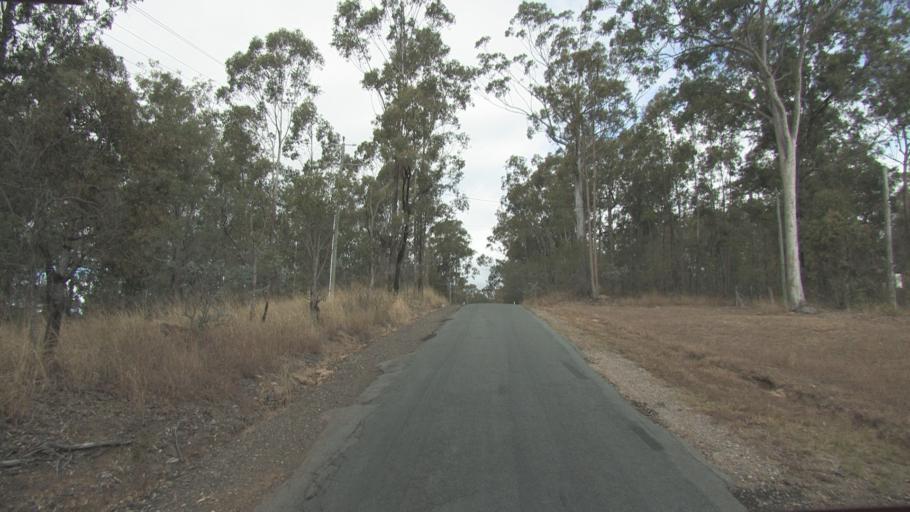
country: AU
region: Queensland
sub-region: Logan
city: Cedar Vale
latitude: -27.8945
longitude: 153.0337
